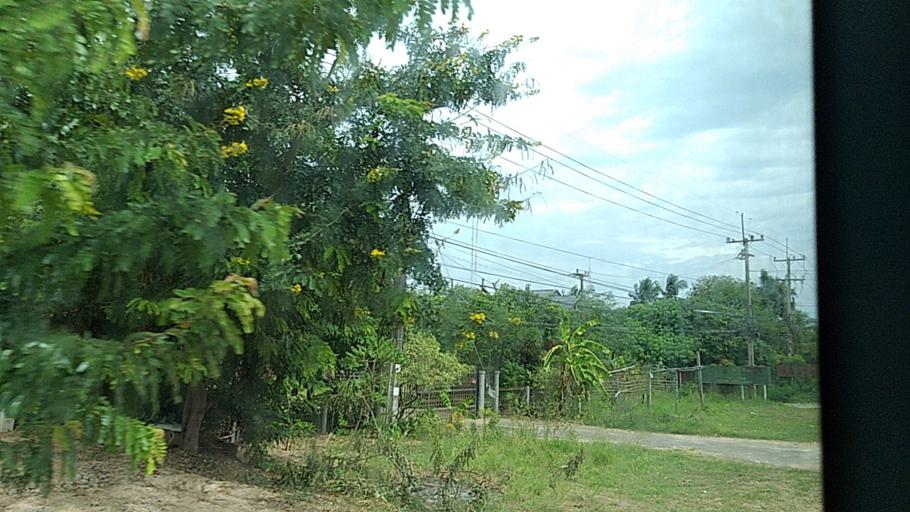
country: TH
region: Maha Sarakham
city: Maha Sarakham
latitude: 16.1518
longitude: 103.3797
